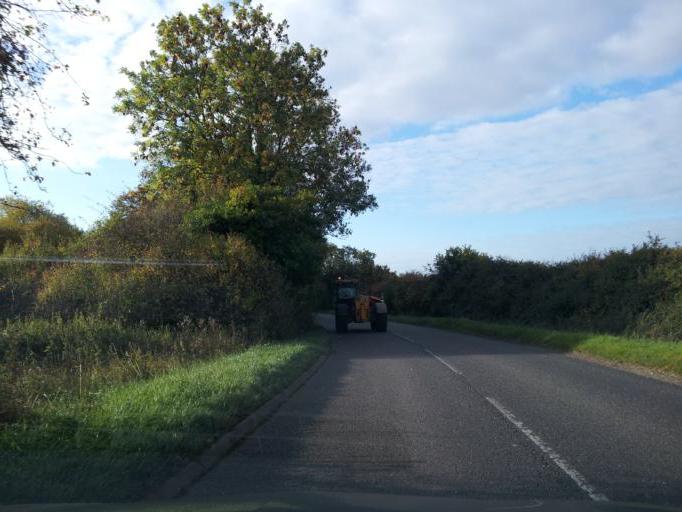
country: GB
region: England
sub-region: Lincolnshire
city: Long Bennington
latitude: 52.9831
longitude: -0.8058
